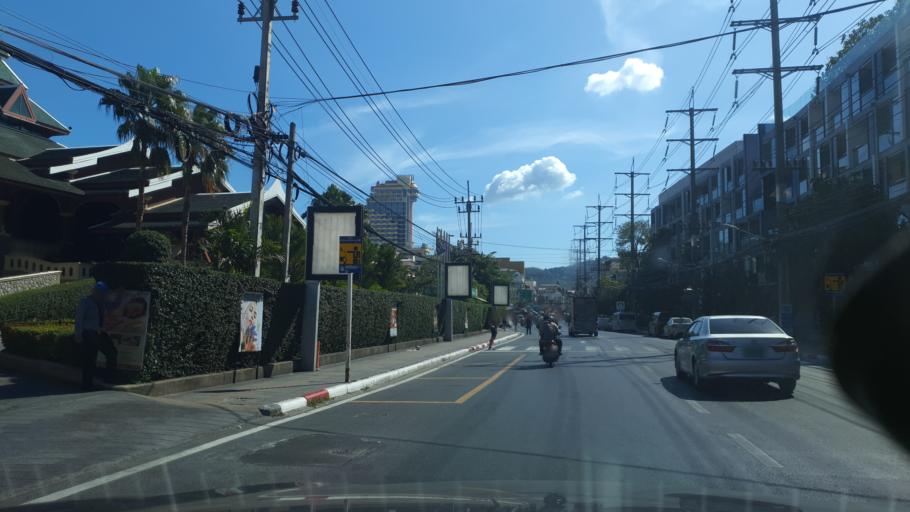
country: TH
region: Phuket
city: Patong
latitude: 7.8994
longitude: 98.3001
